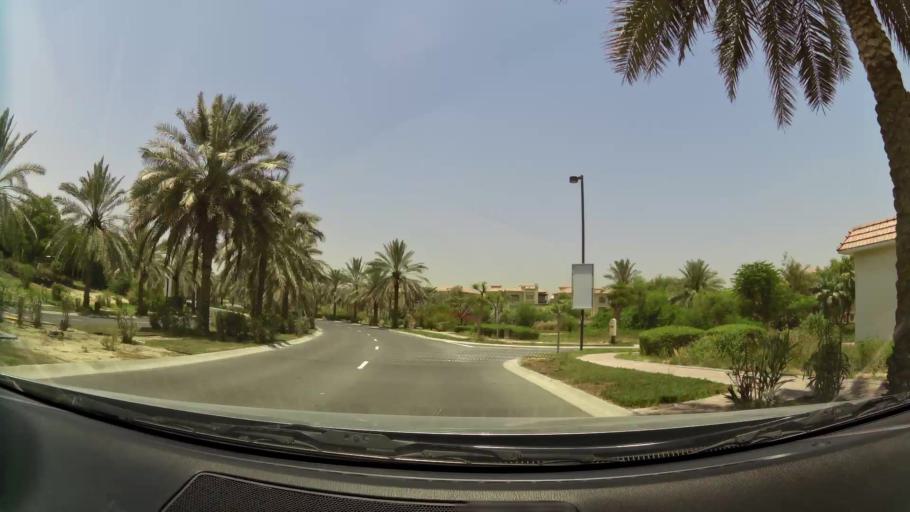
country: AE
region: Dubai
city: Dubai
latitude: 25.0551
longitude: 55.1627
